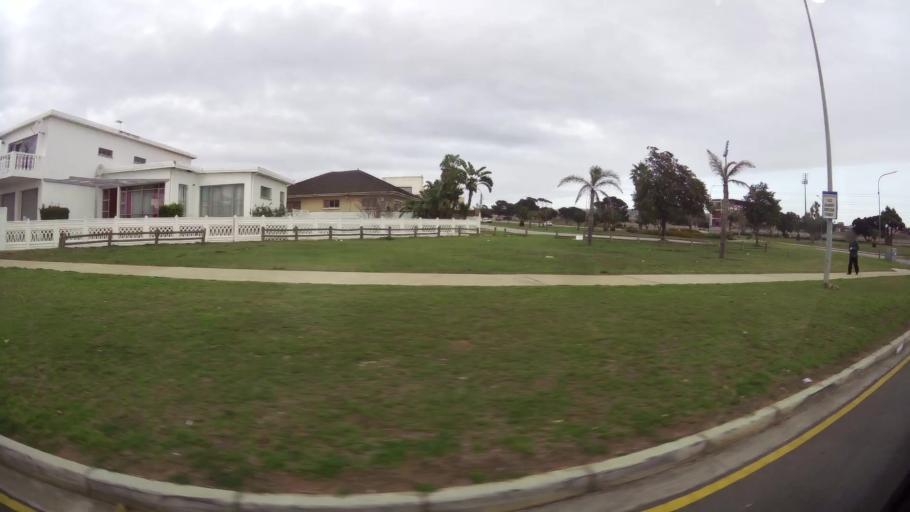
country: ZA
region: Eastern Cape
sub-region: Nelson Mandela Bay Metropolitan Municipality
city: Port Elizabeth
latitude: -33.9155
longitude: 25.5627
